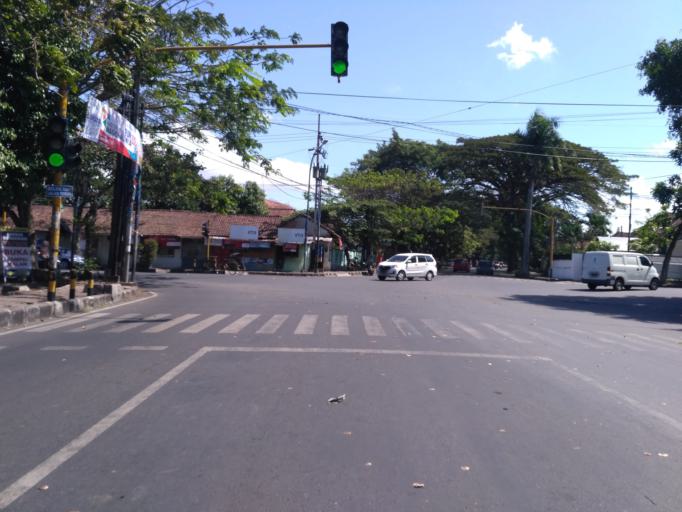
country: ID
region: East Java
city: Malang
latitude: -7.9776
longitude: 112.6437
